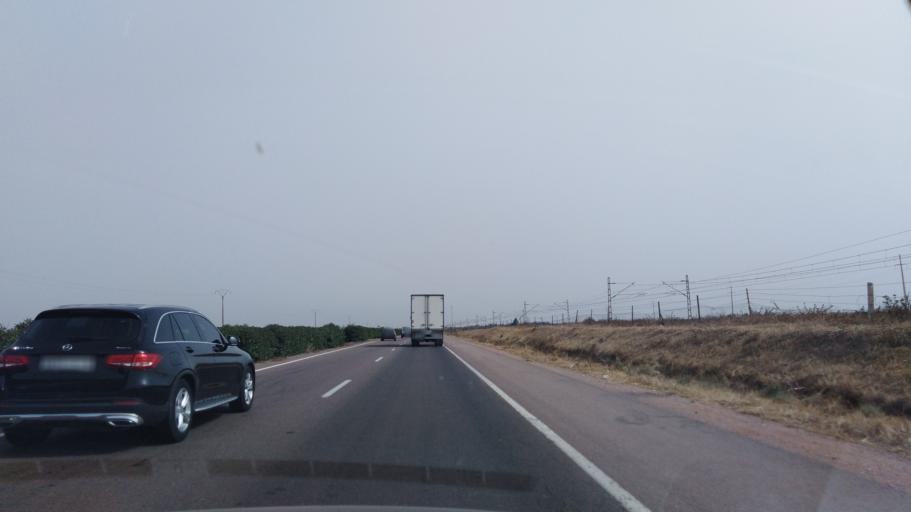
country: MA
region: Chaouia-Ouardigha
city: Nouaseur
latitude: 33.3529
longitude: -7.6168
